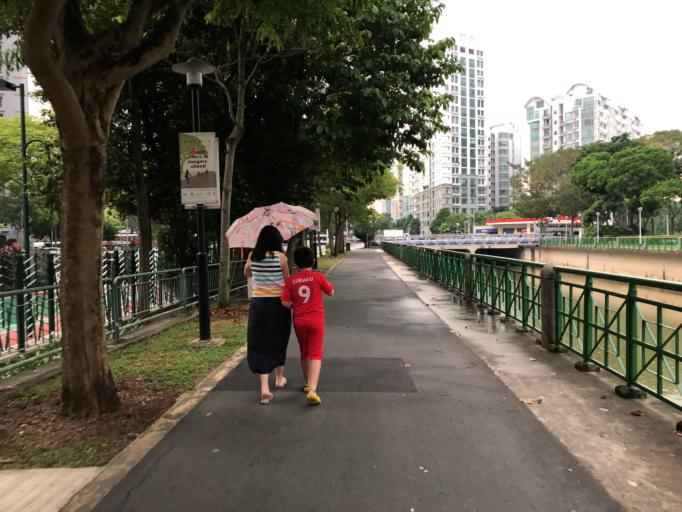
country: SG
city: Singapore
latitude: 1.2927
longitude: 103.8272
